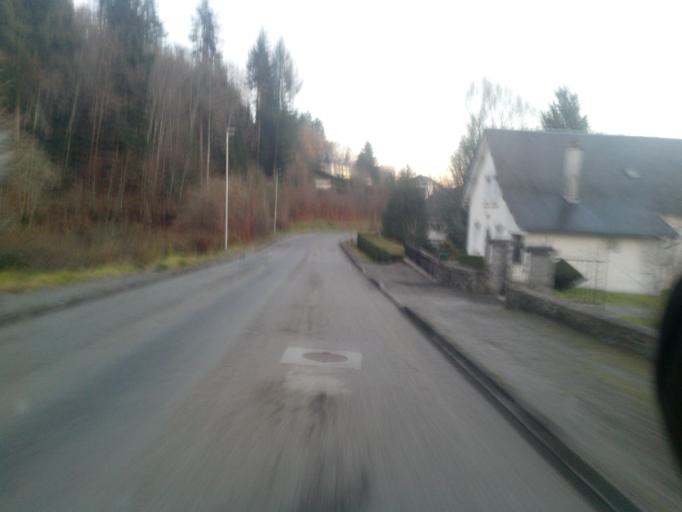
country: FR
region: Limousin
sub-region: Departement de la Correze
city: Meymac
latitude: 45.5423
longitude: 2.1410
